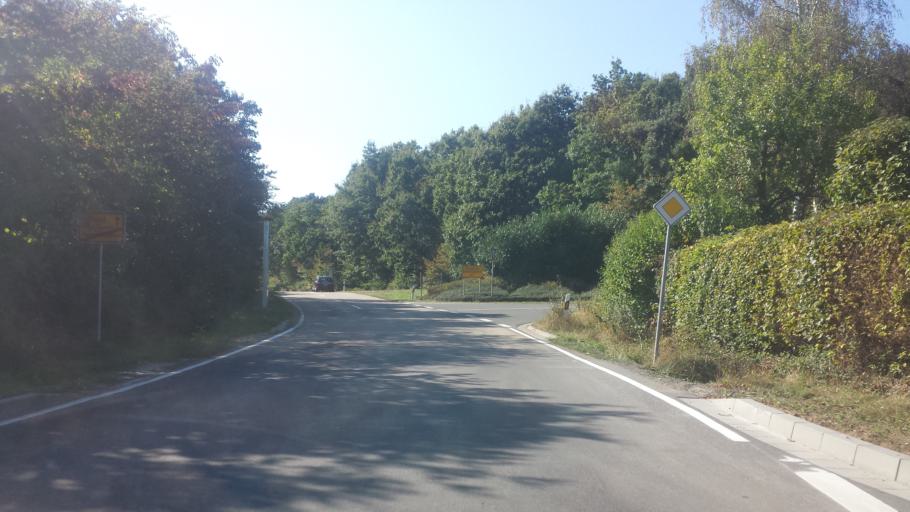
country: DE
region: Rheinland-Pfalz
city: Kerzenheim
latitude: 49.5572
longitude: 8.0395
